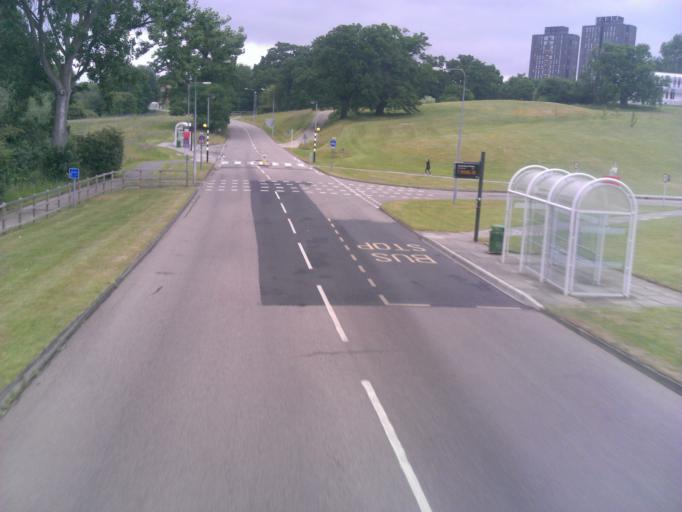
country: GB
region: England
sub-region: Essex
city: Rowhedge
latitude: 51.8752
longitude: 0.9421
